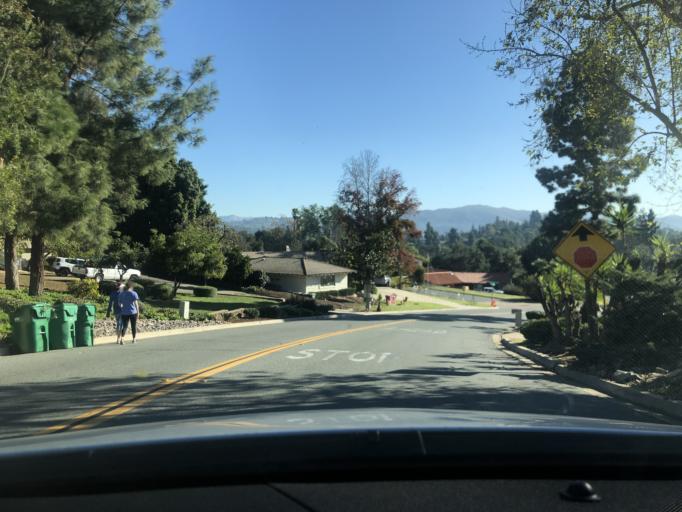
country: US
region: California
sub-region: San Diego County
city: Rancho San Diego
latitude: 32.7699
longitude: -116.9421
